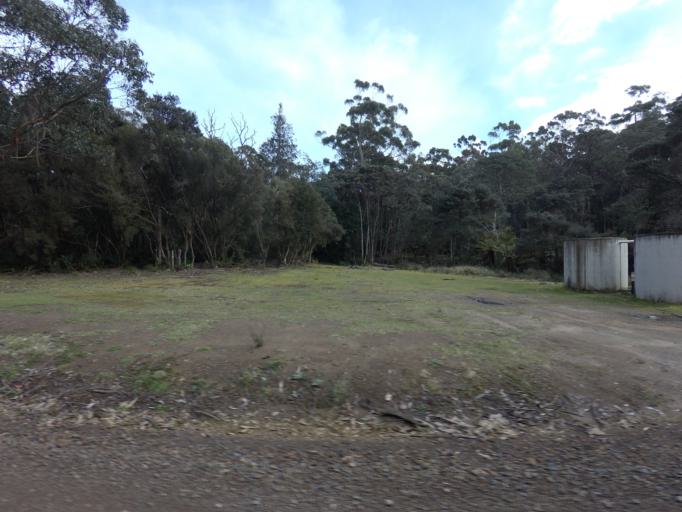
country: AU
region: Tasmania
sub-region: Huon Valley
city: Geeveston
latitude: -43.5426
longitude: 146.8917
